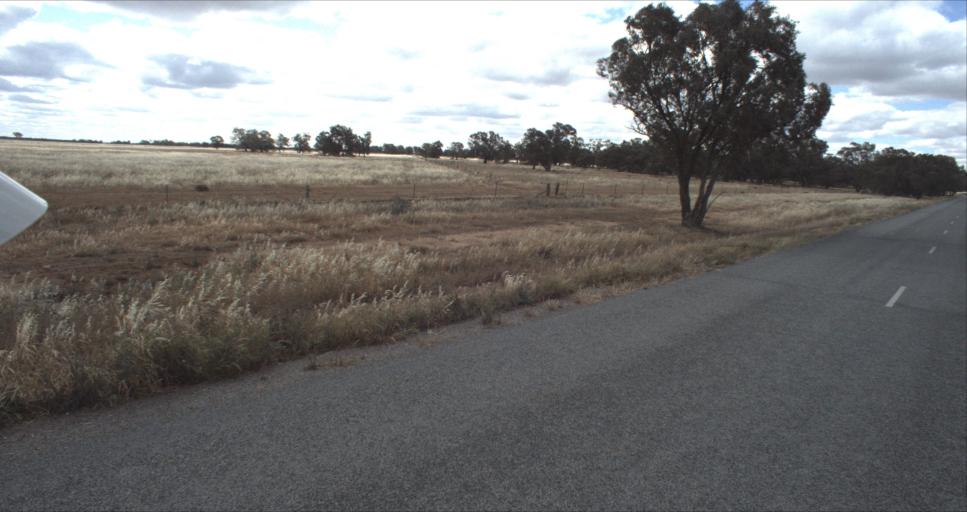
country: AU
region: New South Wales
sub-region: Leeton
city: Leeton
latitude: -34.6942
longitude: 146.3431
